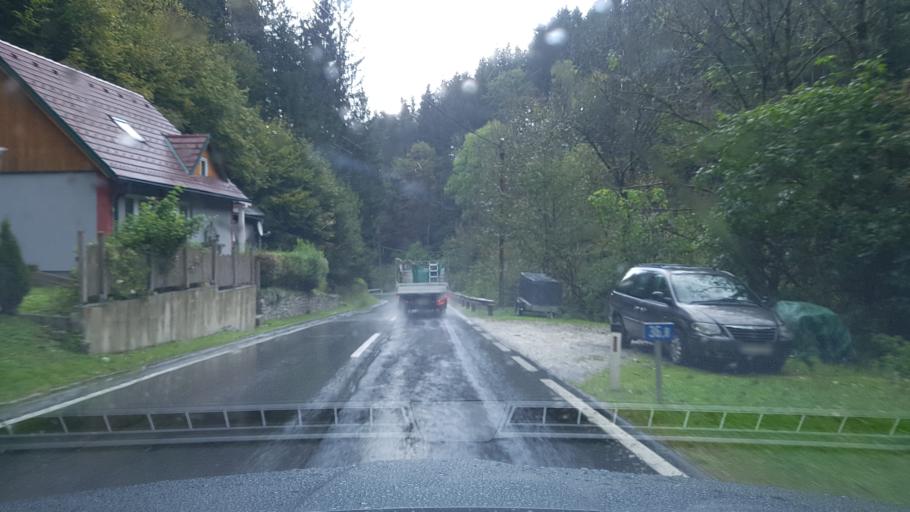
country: AT
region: Styria
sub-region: Politischer Bezirk Voitsberg
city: Salla
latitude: 47.1101
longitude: 14.9793
